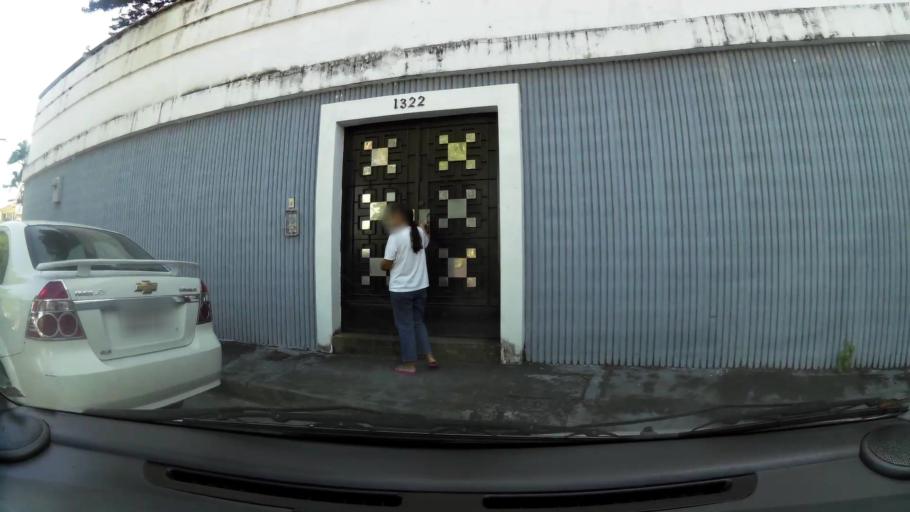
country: EC
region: Guayas
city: Guayaquil
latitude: -2.1644
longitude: -79.9053
